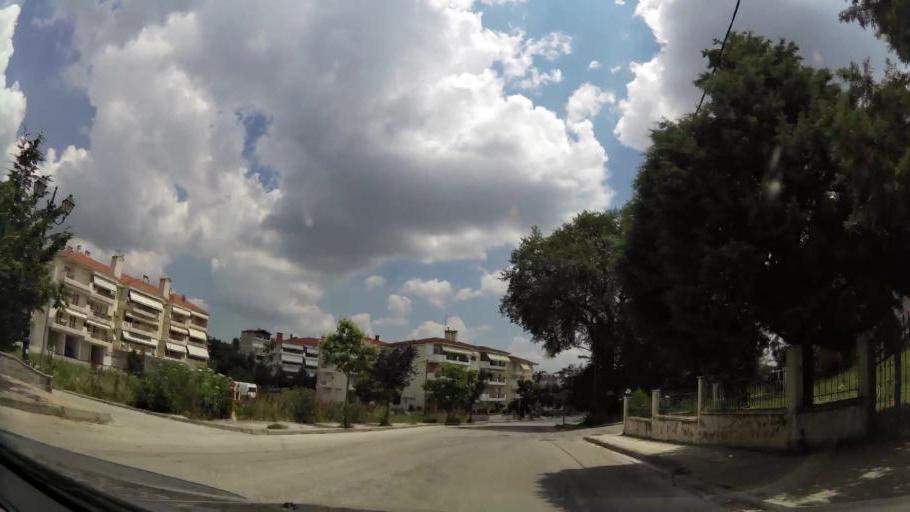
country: GR
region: West Macedonia
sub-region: Nomos Kozanis
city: Kozani
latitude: 40.2916
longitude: 21.7915
